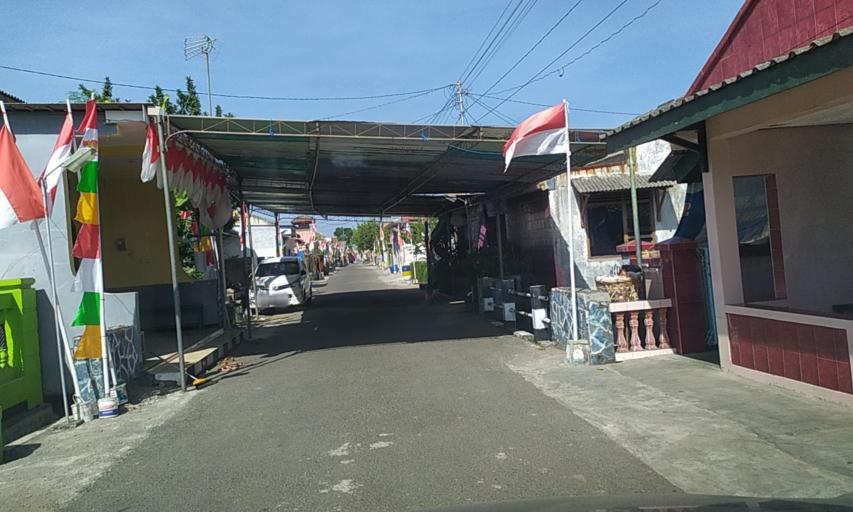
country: ID
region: Central Java
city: Karangbadar Kidul
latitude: -7.7156
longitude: 109.0067
